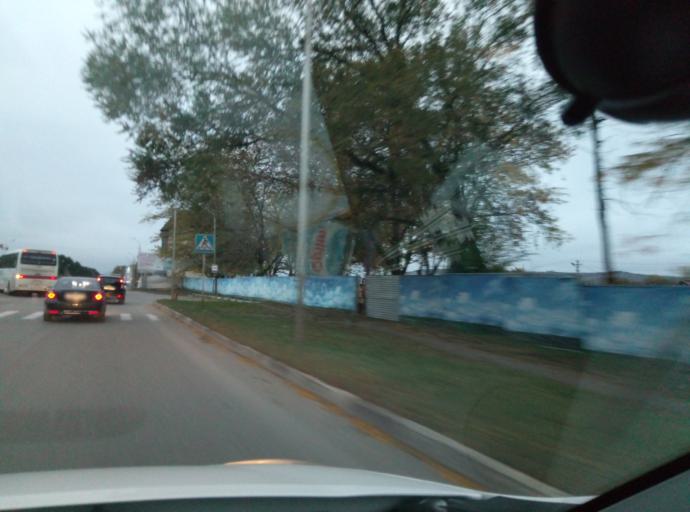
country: RU
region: Stavropol'skiy
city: Yessentukskaya
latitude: 44.0543
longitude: 42.9083
